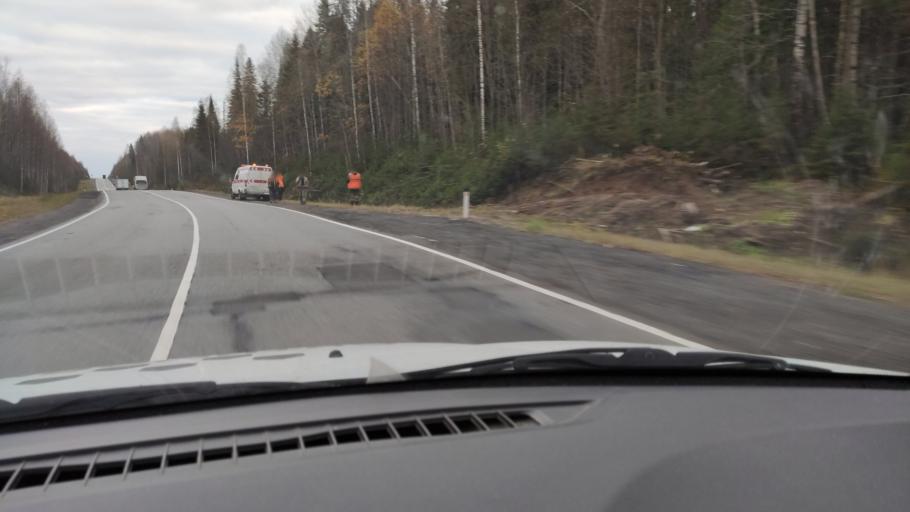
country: RU
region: Kirov
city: Chernaya Kholunitsa
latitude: 58.8587
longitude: 51.6289
